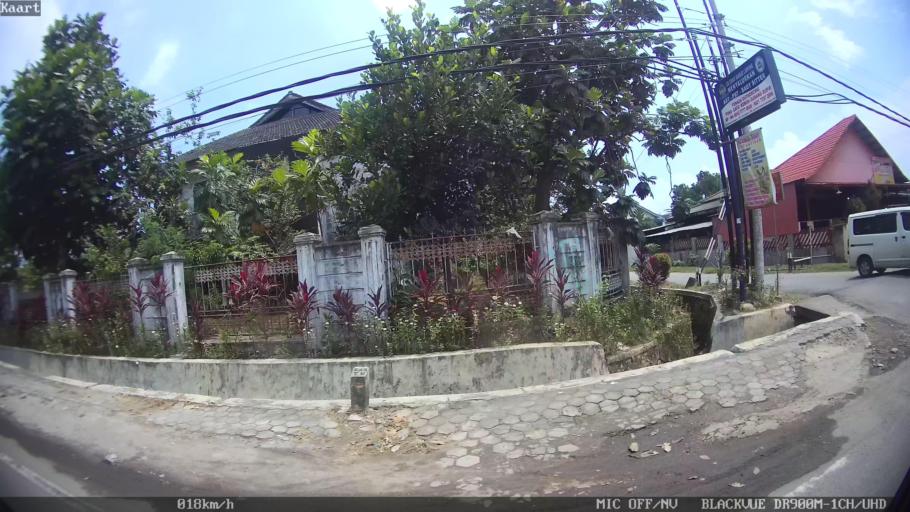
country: ID
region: Lampung
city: Kedaton
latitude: -5.3822
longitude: 105.2758
